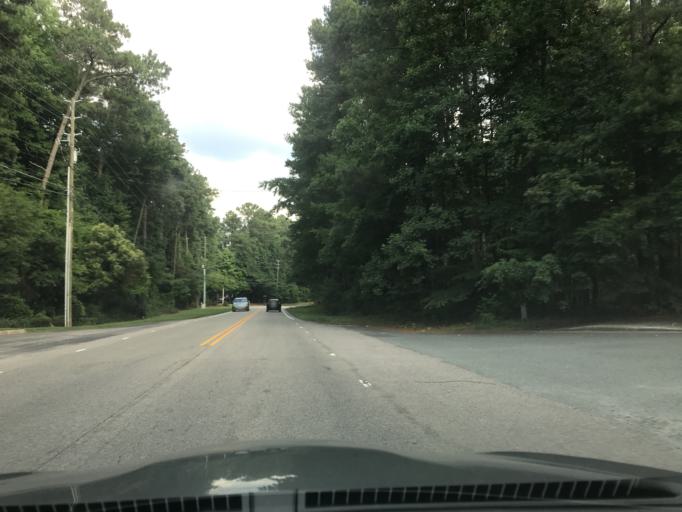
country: US
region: North Carolina
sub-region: Wake County
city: West Raleigh
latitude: 35.8763
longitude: -78.7030
